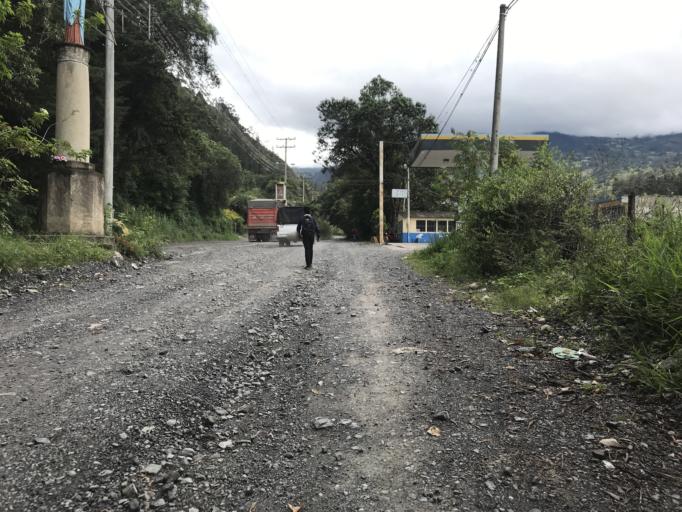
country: CO
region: Boyaca
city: Boavita
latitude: 6.3271
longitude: -72.5810
